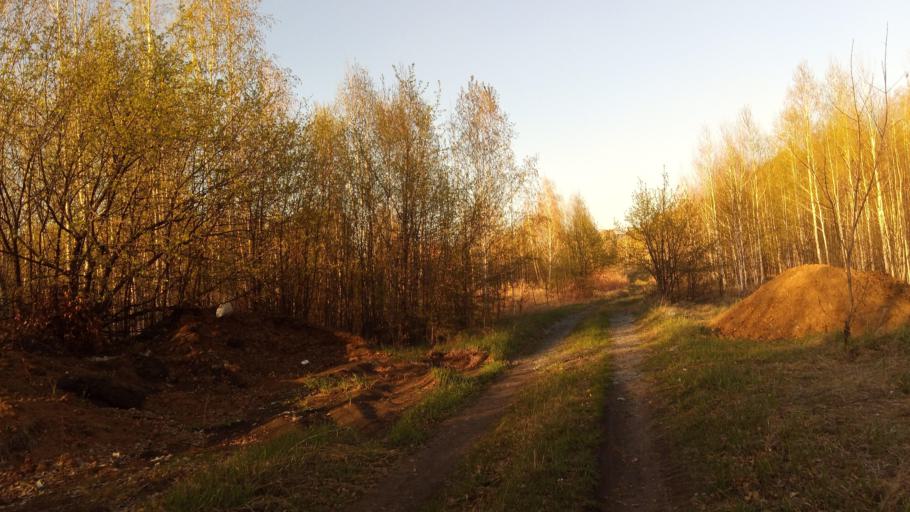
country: RU
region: Chelyabinsk
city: Timiryazevskiy
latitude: 54.9905
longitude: 60.8610
